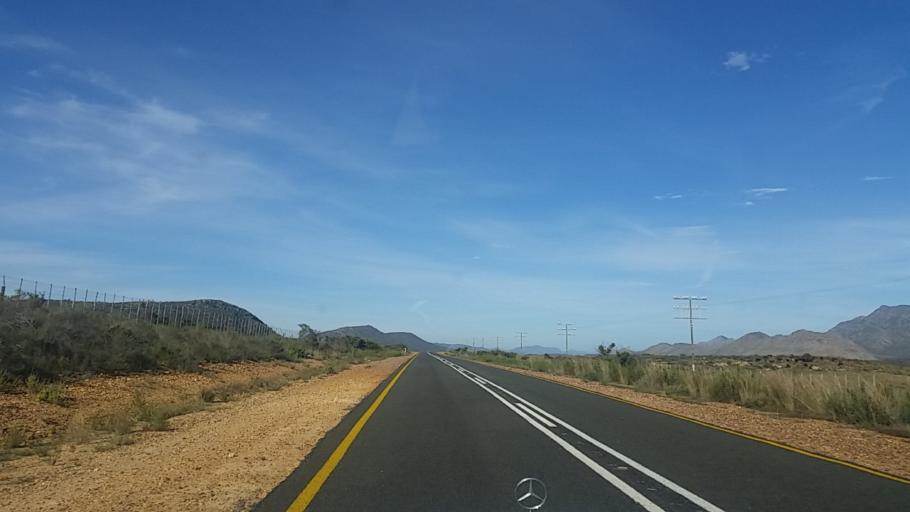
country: ZA
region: Western Cape
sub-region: Eden District Municipality
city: George
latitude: -33.7820
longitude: 22.6765
